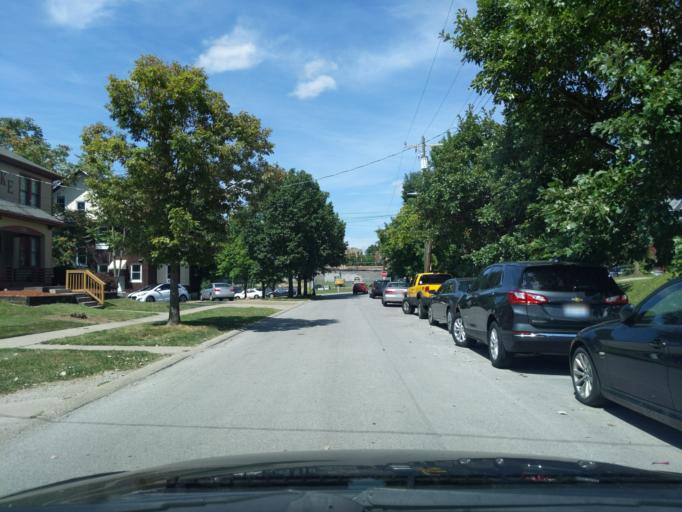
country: US
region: Ohio
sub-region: Hamilton County
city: Saint Bernard
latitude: 39.1337
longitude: -84.5218
